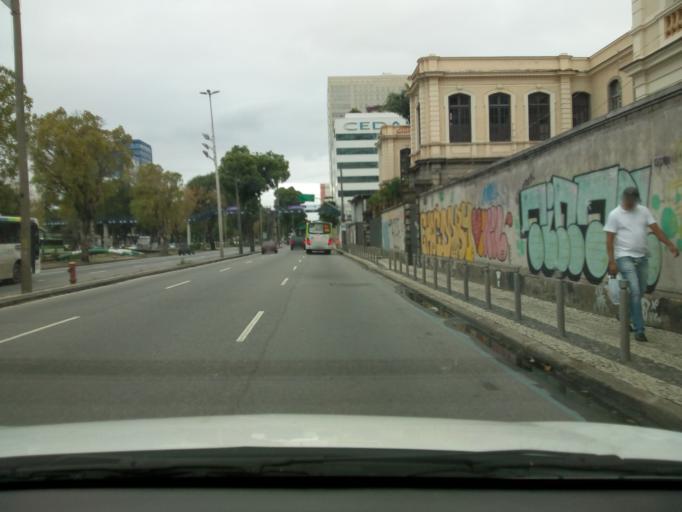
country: BR
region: Rio de Janeiro
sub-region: Rio De Janeiro
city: Rio de Janeiro
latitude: -22.9090
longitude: -43.2020
